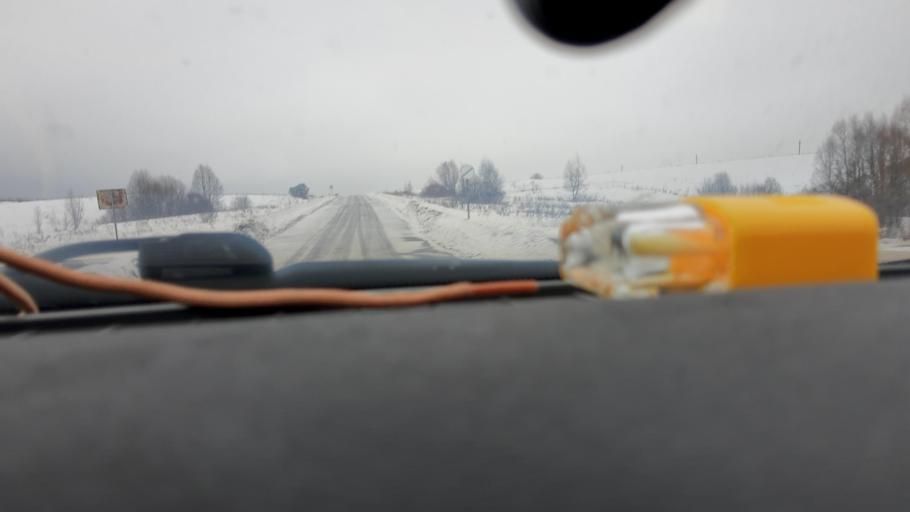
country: RU
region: Bashkortostan
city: Iglino
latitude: 54.6399
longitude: 56.4234
